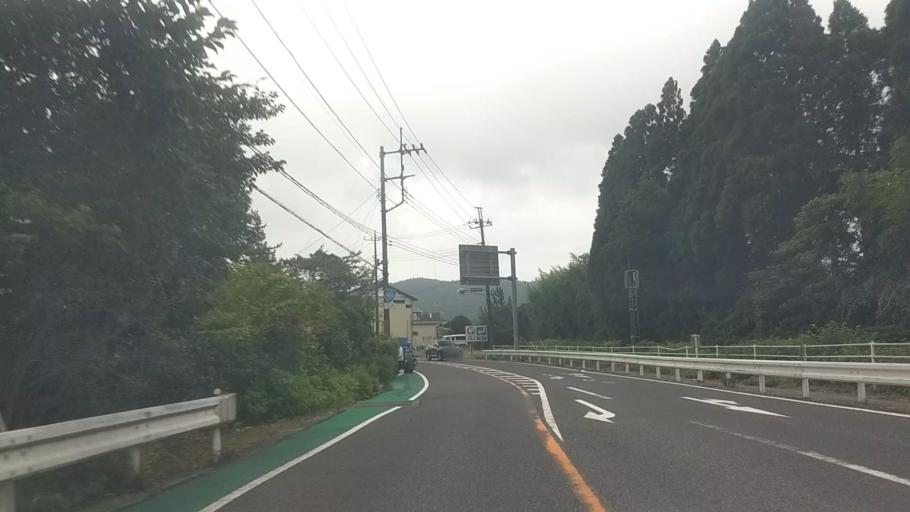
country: JP
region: Chiba
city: Ohara
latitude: 35.2817
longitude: 140.3063
